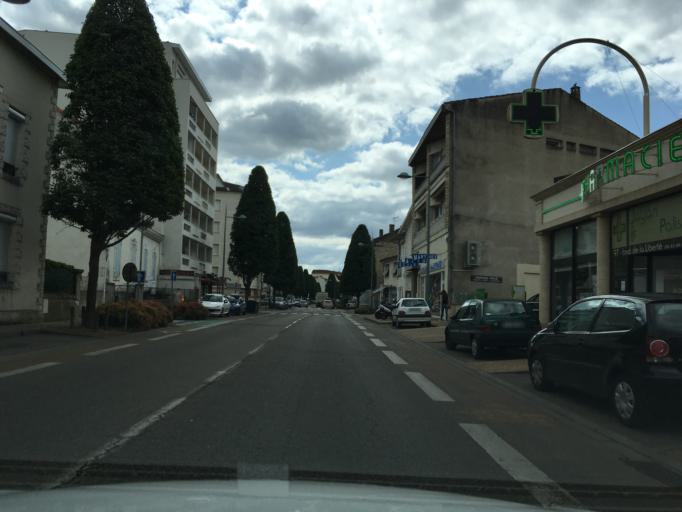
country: FR
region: Aquitaine
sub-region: Departement du Lot-et-Garonne
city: Agen
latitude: 44.1991
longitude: 0.6213
